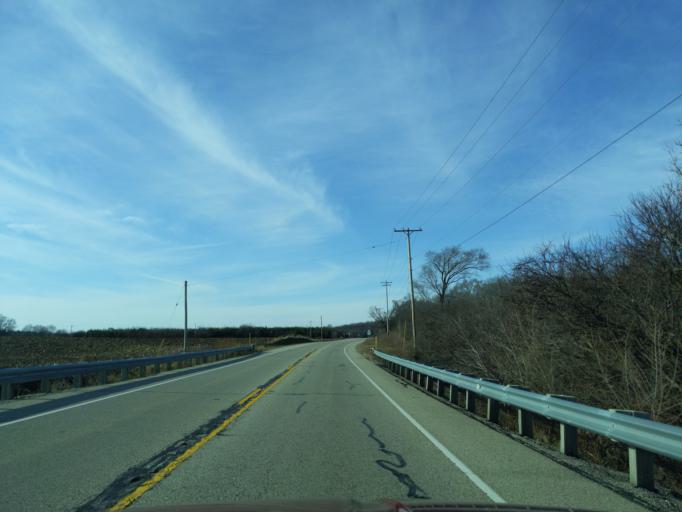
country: US
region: Wisconsin
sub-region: Jefferson County
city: Palmyra
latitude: 42.7972
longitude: -88.6370
